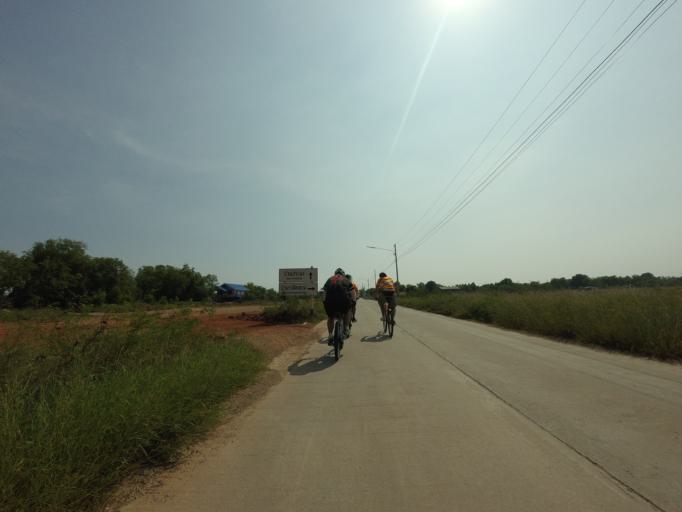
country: TH
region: Samut Sakhon
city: Samut Sakhon
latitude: 13.5028
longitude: 100.3856
